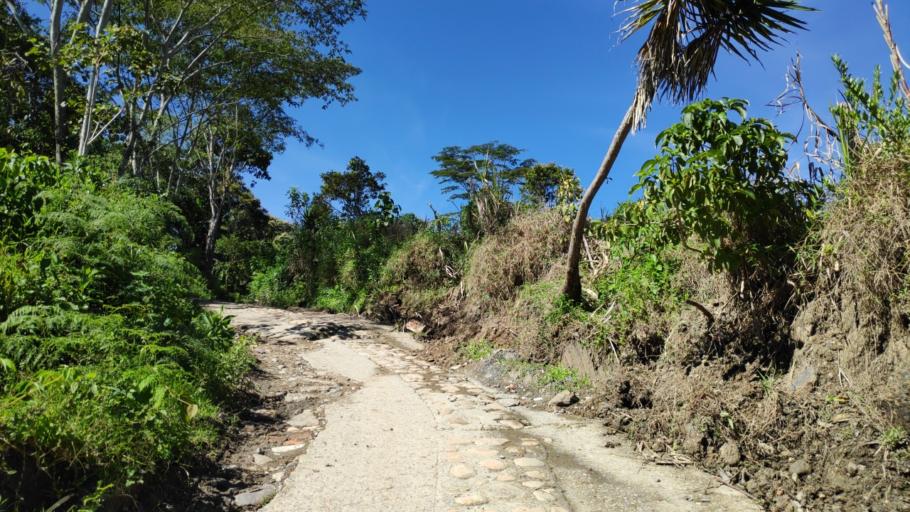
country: CO
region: Santander
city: Guepsa
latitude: 5.9880
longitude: -73.5434
